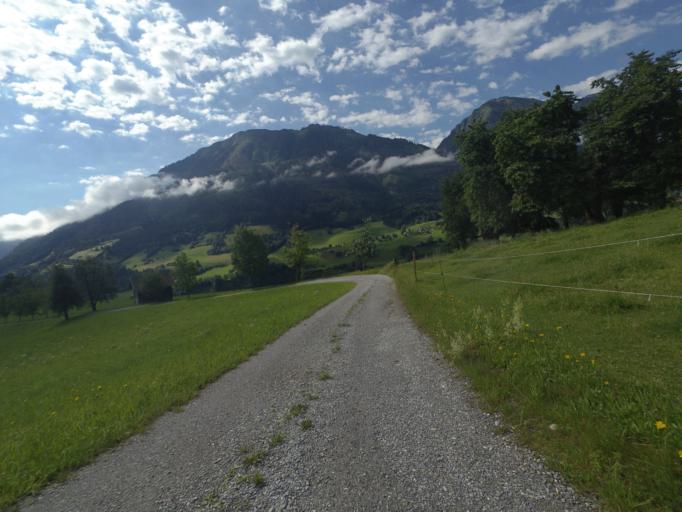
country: AT
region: Salzburg
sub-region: Politischer Bezirk Sankt Johann im Pongau
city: Schwarzach im Pongau
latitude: 47.3224
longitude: 13.1363
